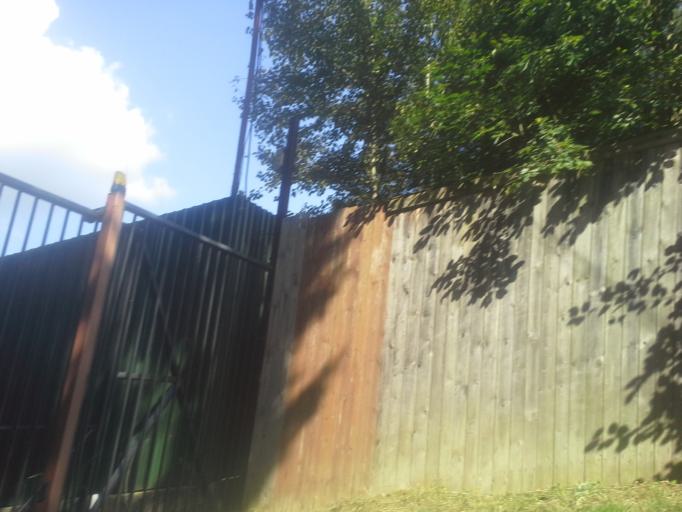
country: RU
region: Moskovskaya
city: Selyatino
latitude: 55.4660
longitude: 36.9897
